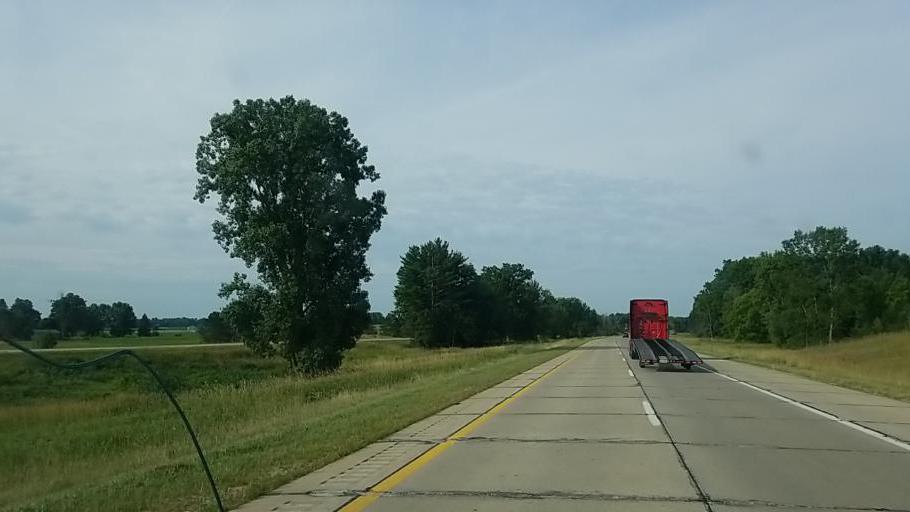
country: US
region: Michigan
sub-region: Eaton County
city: Olivet
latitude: 42.4818
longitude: -84.8787
